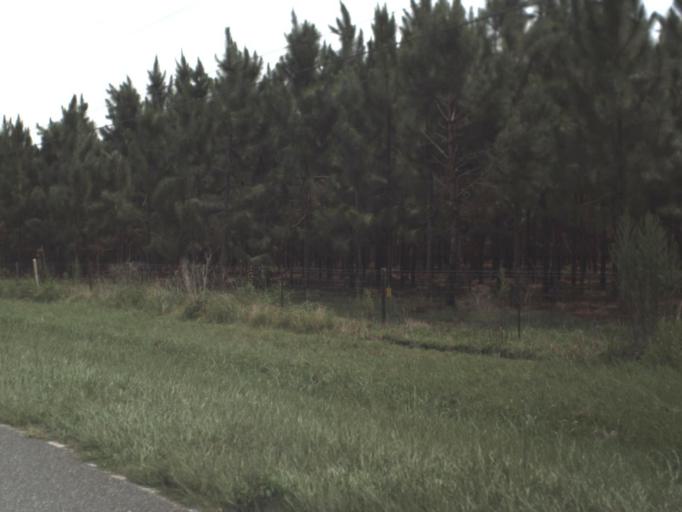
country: US
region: Florida
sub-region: Columbia County
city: Watertown
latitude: 30.0584
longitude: -82.5994
